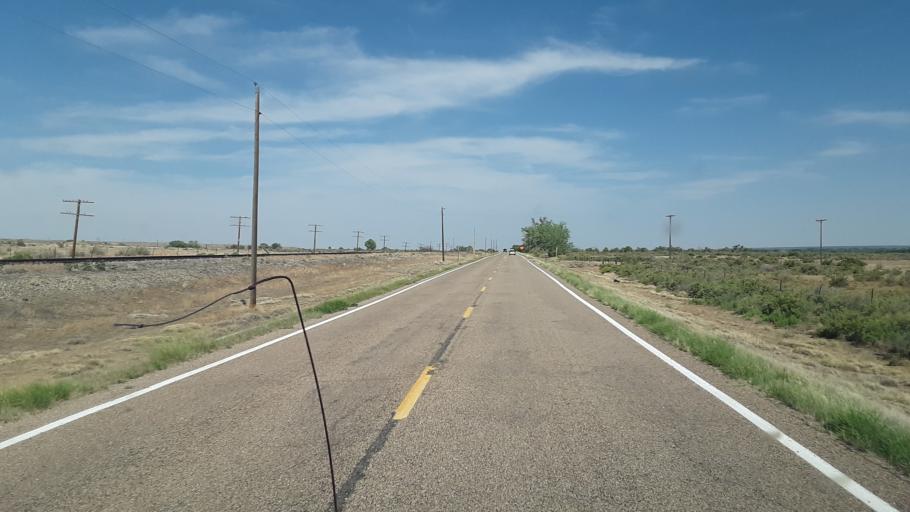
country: US
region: Colorado
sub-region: Otero County
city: Fowler
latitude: 38.1601
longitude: -104.0429
